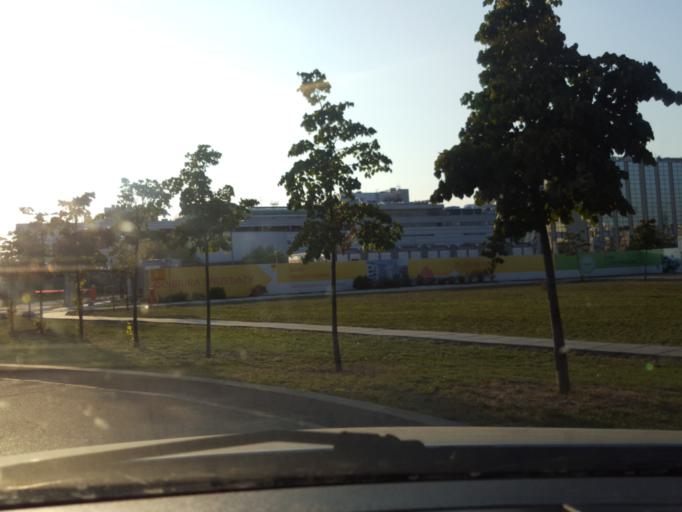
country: PL
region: Masovian Voivodeship
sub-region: Warszawa
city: Praga Poludnie
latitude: 52.2300
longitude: 21.1090
